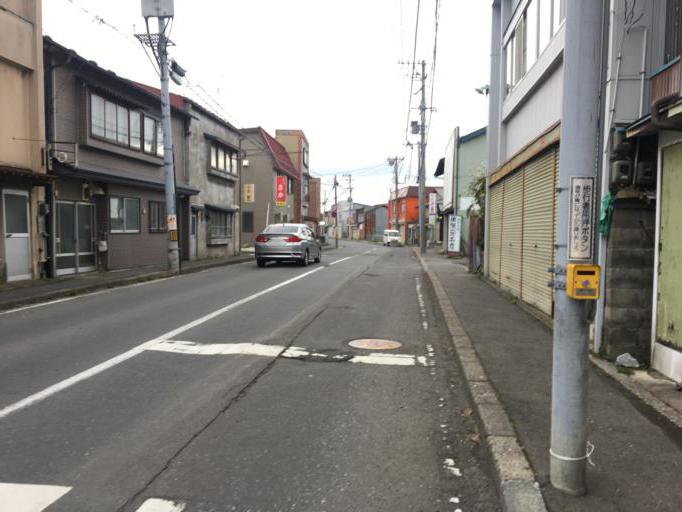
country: JP
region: Aomori
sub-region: Hachinohe Shi
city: Uchimaru
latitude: 40.5213
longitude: 141.5179
